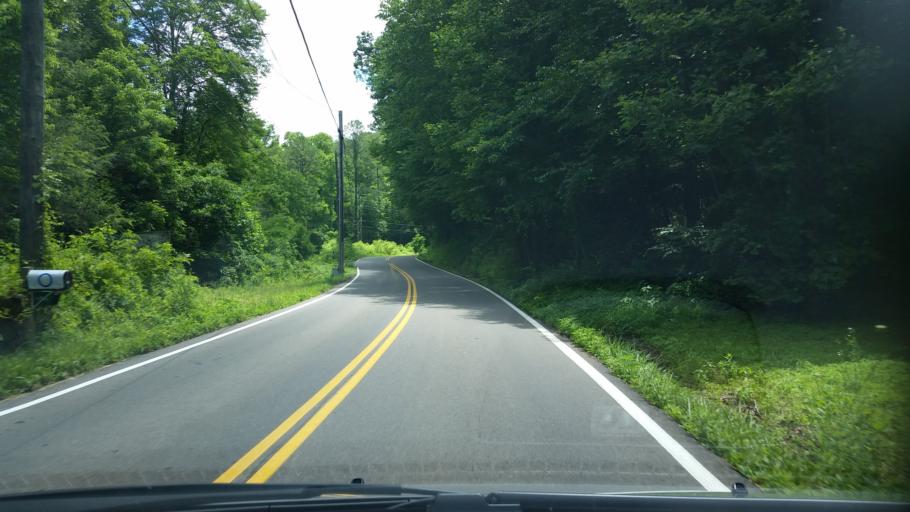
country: US
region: Tennessee
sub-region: Sevier County
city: Gatlinburg
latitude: 35.7479
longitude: -83.4339
